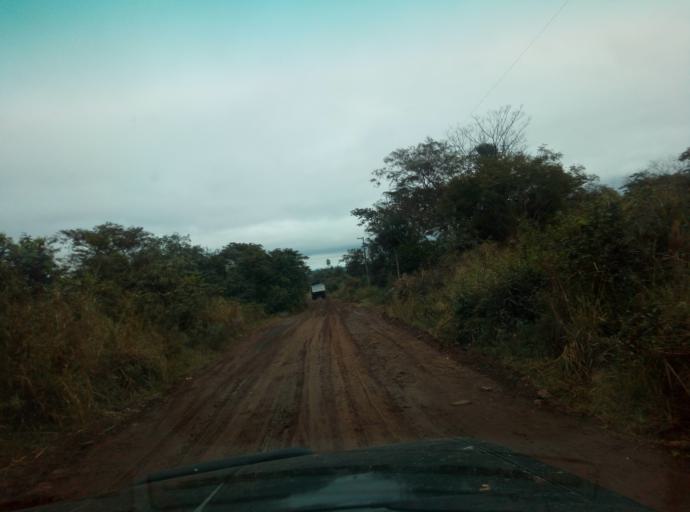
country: PY
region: Caaguazu
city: Carayao
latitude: -25.1903
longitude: -56.3775
